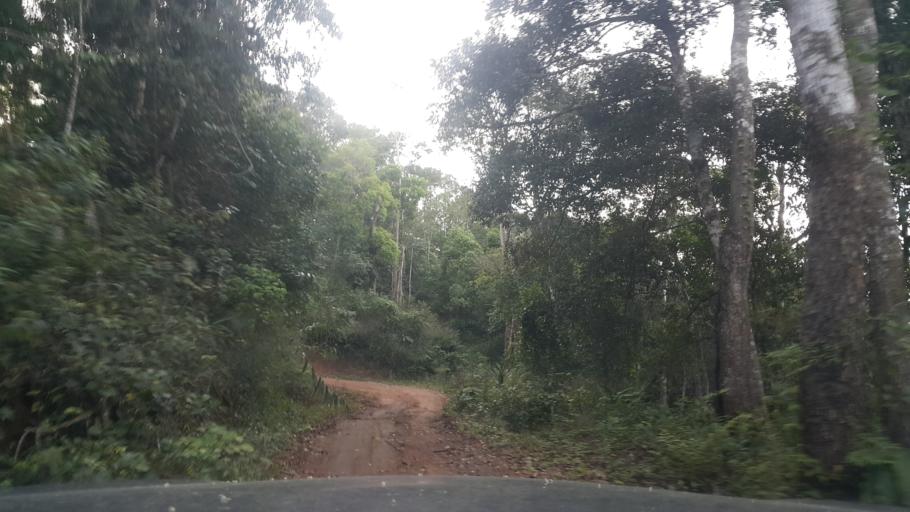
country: TH
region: Chiang Mai
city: Samoeng
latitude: 19.0315
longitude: 98.6479
